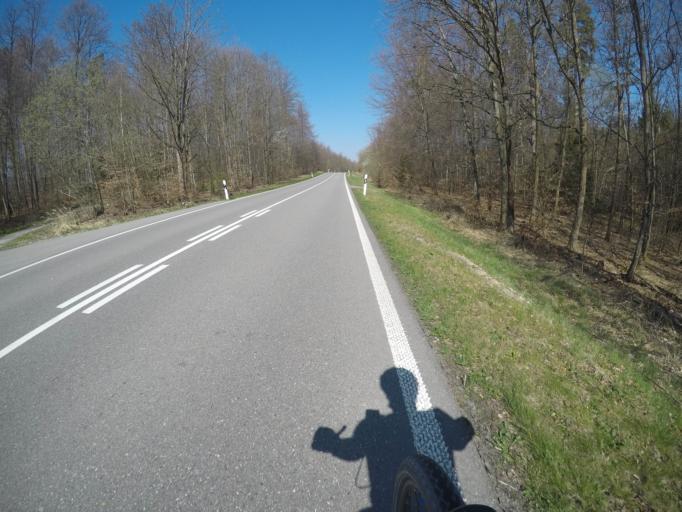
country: DE
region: Baden-Wuerttemberg
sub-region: Regierungsbezirk Stuttgart
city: Leonberg
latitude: 48.7565
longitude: 9.0150
